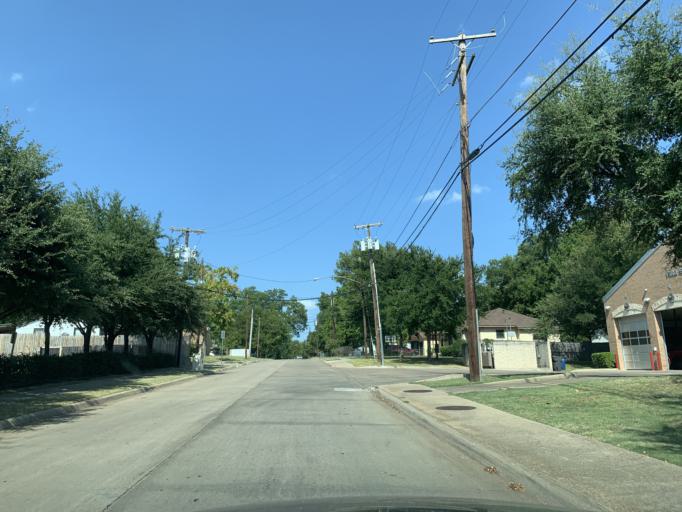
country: US
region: Texas
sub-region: Dallas County
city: Hutchins
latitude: 32.6842
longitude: -96.7880
